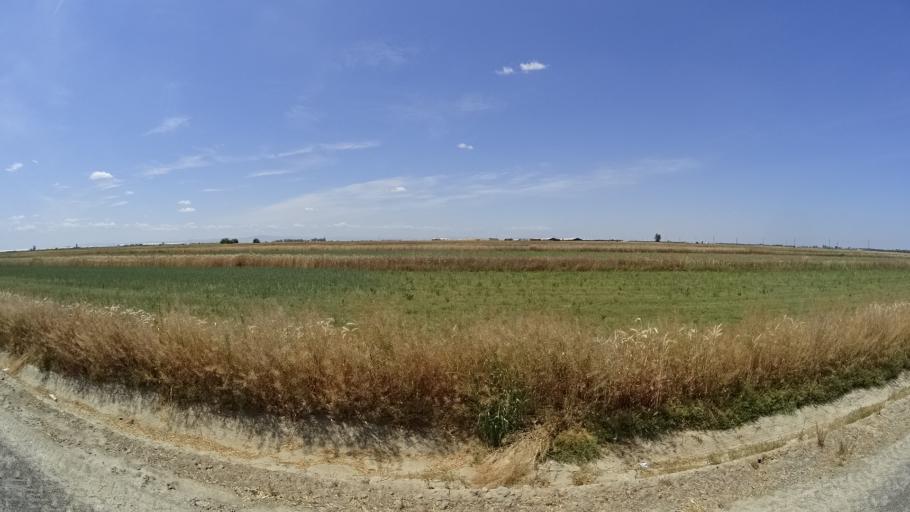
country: US
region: California
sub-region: Kings County
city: Home Garden
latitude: 36.2214
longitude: -119.6728
